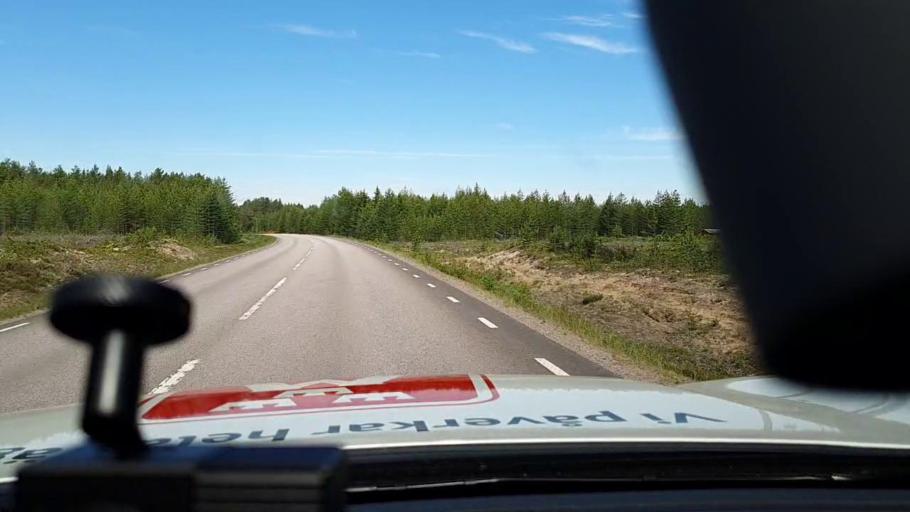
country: SE
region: Norrbotten
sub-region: Lulea Kommun
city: Sodra Sunderbyn
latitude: 65.6333
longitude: 21.9222
